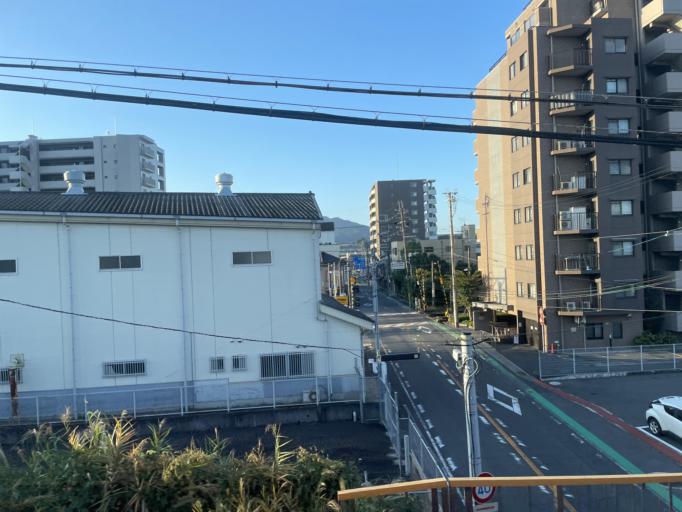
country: JP
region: Nara
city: Sakurai
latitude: 34.5132
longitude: 135.8435
